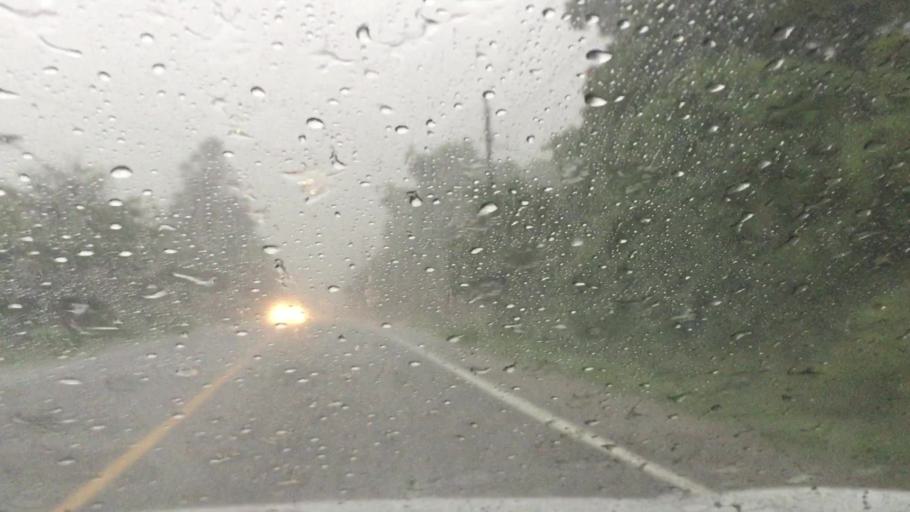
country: CA
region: Ontario
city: Markham
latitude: 43.8622
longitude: -79.2051
